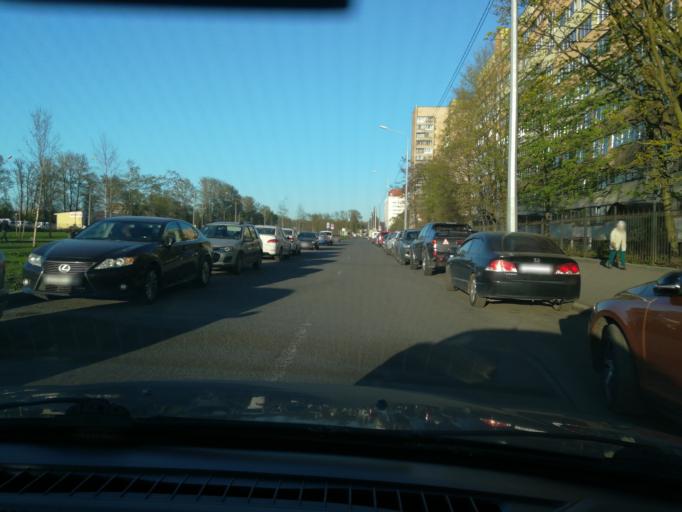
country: RU
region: St.-Petersburg
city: Avtovo
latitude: 59.8628
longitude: 30.2459
